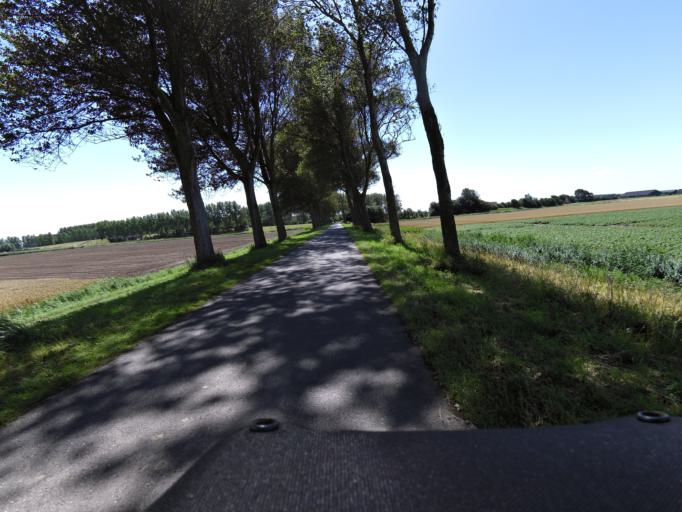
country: NL
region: South Holland
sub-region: Gemeente Goeree-Overflakkee
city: Goedereede
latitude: 51.8159
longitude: 4.0209
